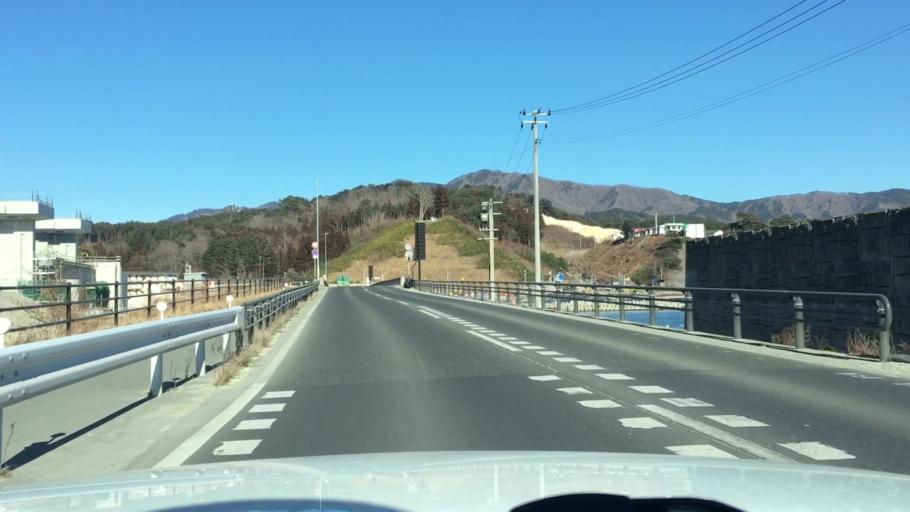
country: JP
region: Iwate
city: Yamada
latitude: 39.4728
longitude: 141.9543
